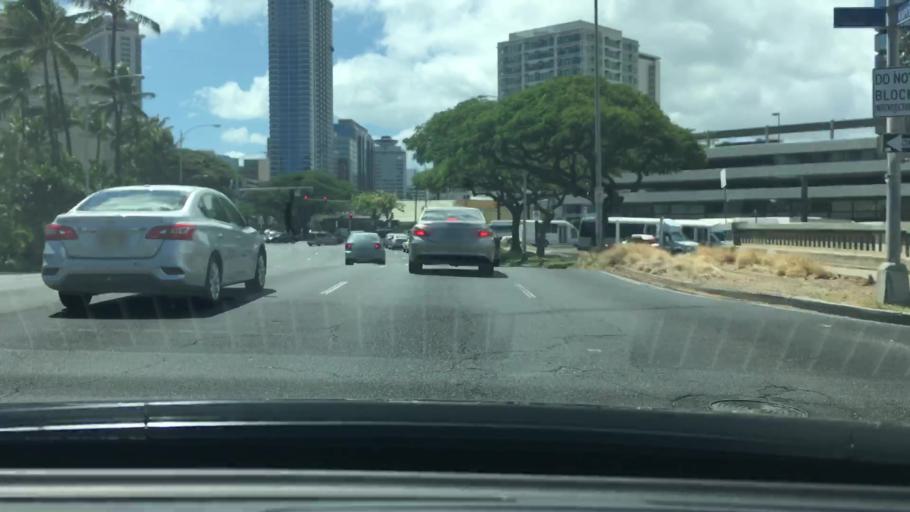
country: US
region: Hawaii
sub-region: Honolulu County
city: Honolulu
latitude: 21.2904
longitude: -157.8346
